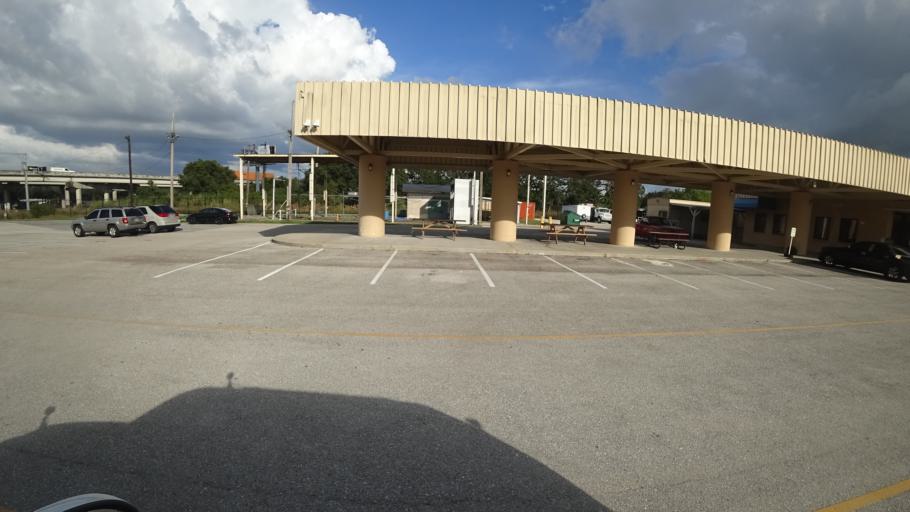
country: US
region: Florida
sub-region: Manatee County
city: West Samoset
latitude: 27.4761
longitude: -82.5508
